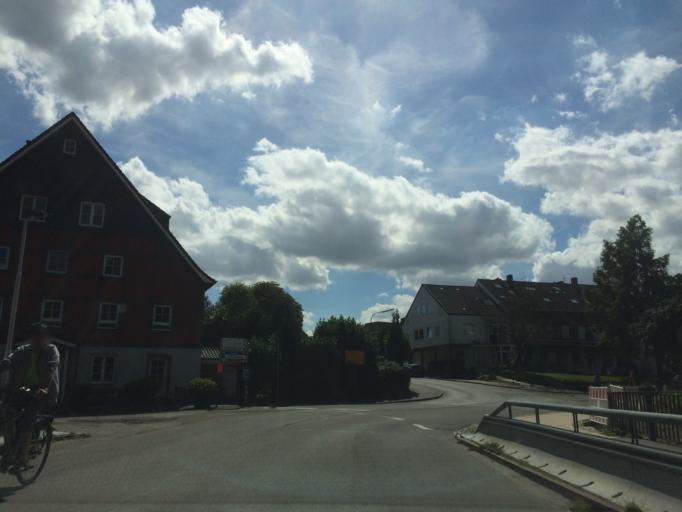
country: DE
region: Schleswig-Holstein
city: Malente
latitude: 54.1660
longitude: 10.5488
